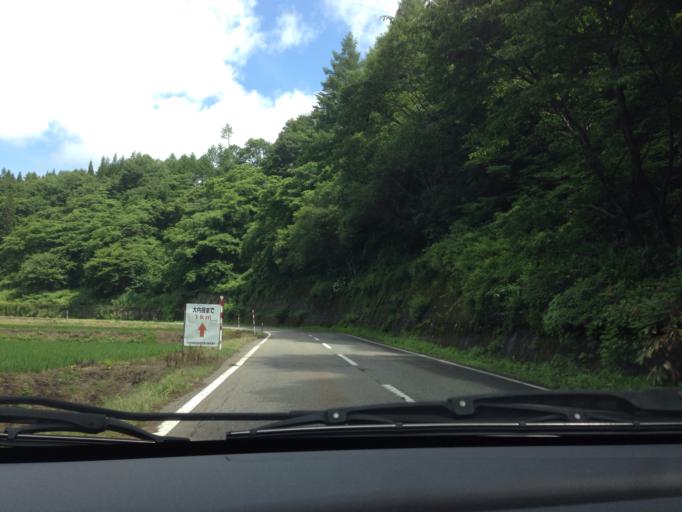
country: JP
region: Fukushima
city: Kitakata
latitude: 37.3229
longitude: 139.8647
